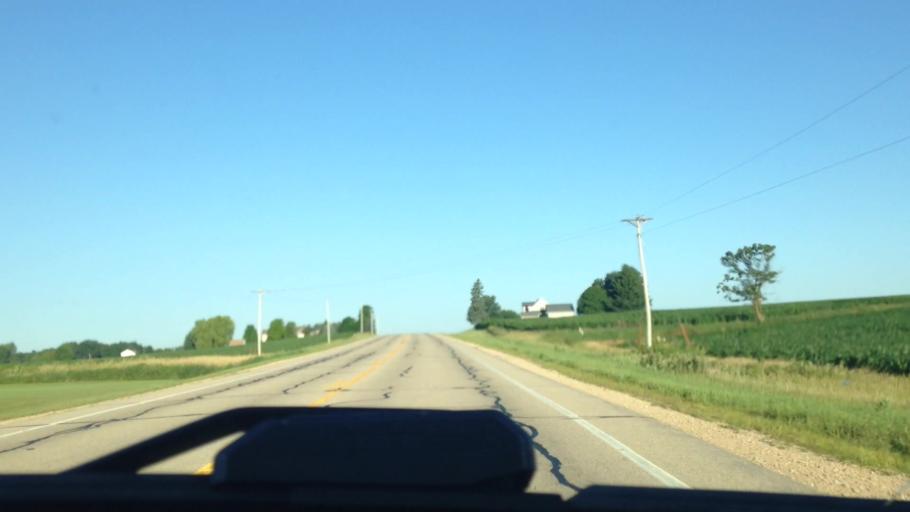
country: US
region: Wisconsin
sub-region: Columbia County
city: Fall River
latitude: 43.3412
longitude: -89.1006
